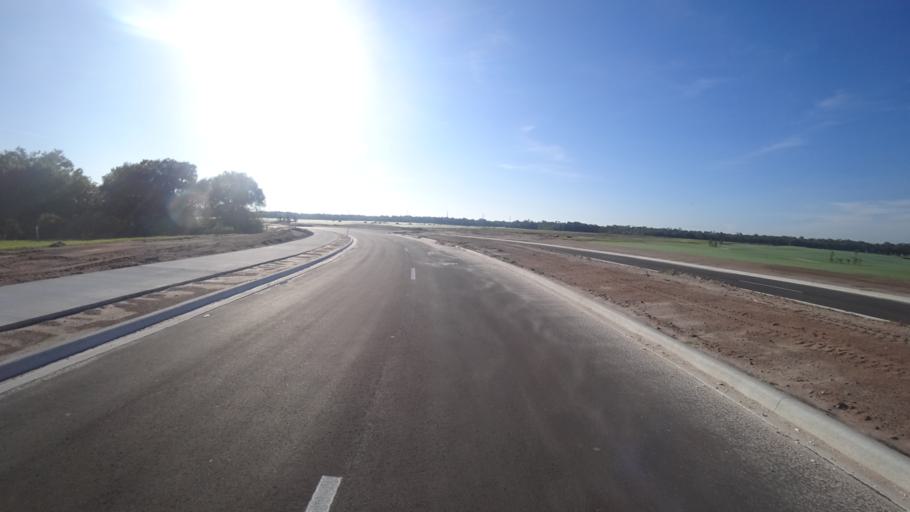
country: US
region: Florida
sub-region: Sarasota County
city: The Meadows
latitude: 27.4344
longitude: -82.3562
